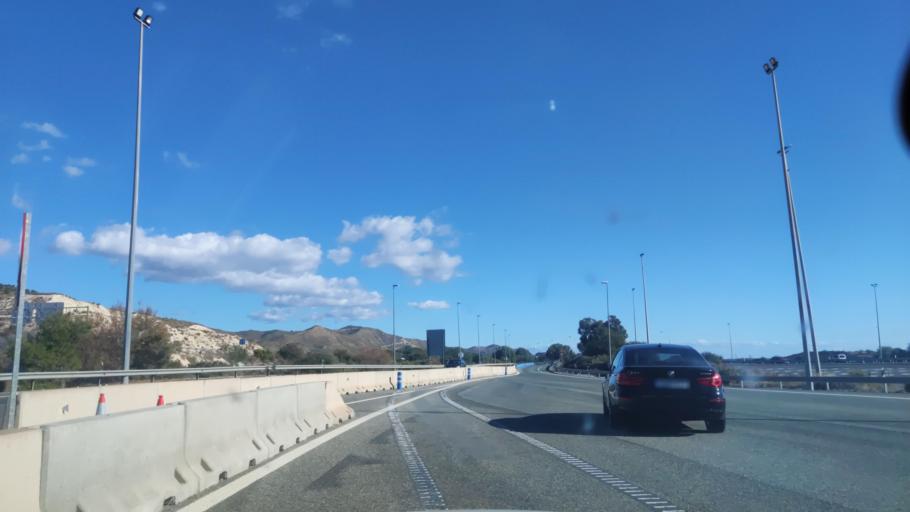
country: ES
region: Valencia
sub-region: Provincia de Alicante
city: el Campello
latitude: 38.4409
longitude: -0.4002
